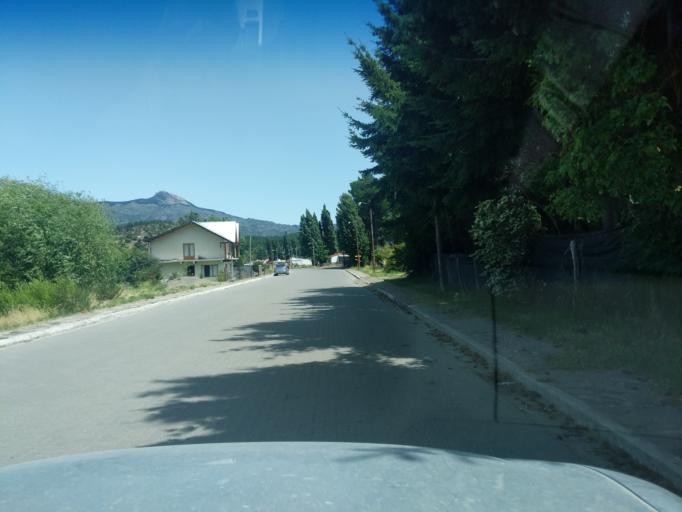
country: CL
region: Los Lagos
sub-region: Provincia de Palena
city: Palena
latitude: -43.5357
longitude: -71.4711
